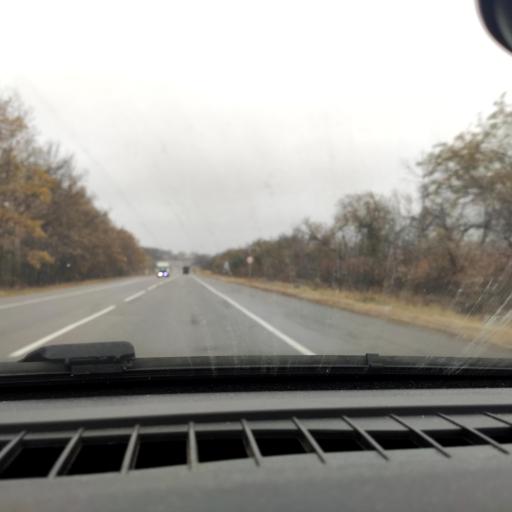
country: RU
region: Voronezj
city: Kolodeznyy
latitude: 51.3303
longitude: 39.0262
